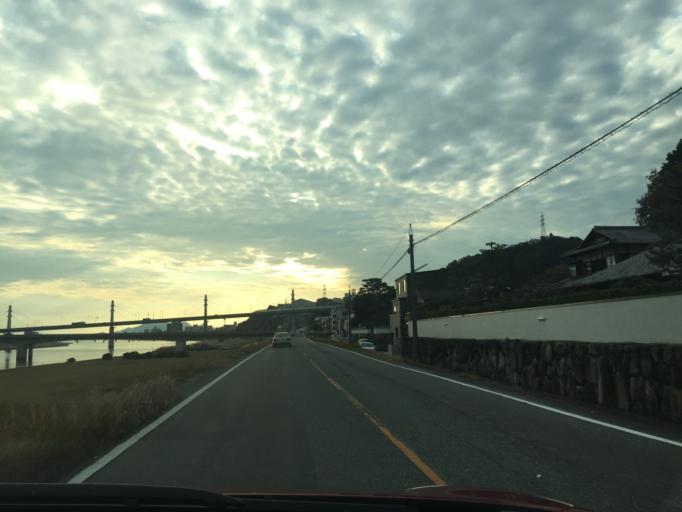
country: JP
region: Hiroshima
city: Hiroshima-shi
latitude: 34.4084
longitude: 132.4406
